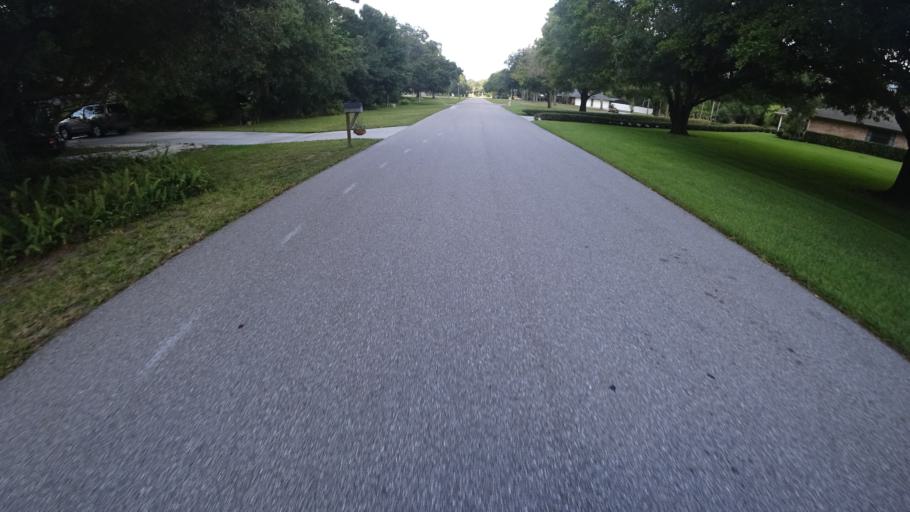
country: US
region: Florida
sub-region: Sarasota County
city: The Meadows
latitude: 27.4315
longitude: -82.4447
